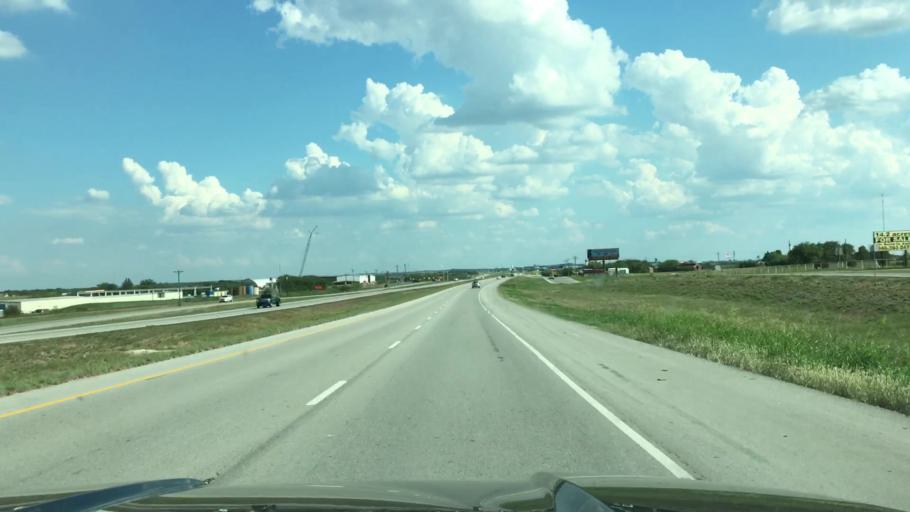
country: US
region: Texas
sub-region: Wise County
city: Decatur
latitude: 33.2019
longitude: -97.5656
